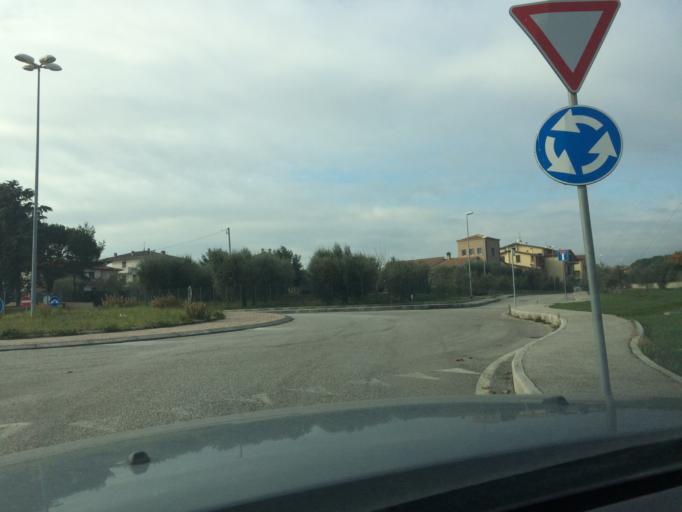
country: IT
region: Umbria
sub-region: Provincia di Perugia
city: Via Lippia
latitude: 43.0884
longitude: 12.4854
